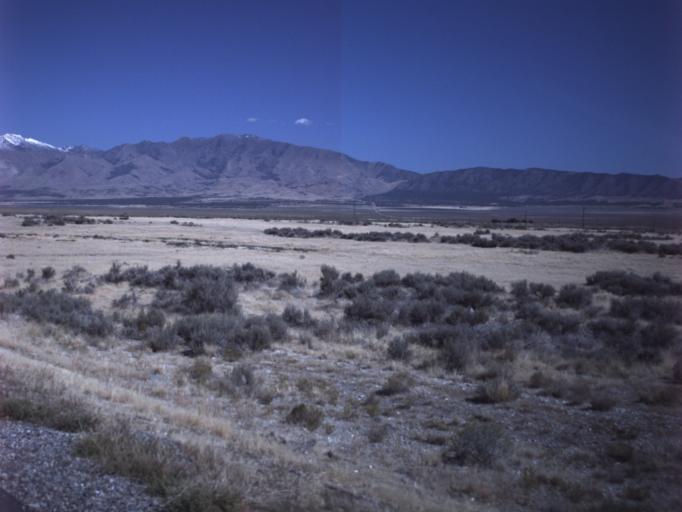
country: US
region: Utah
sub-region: Tooele County
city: Grantsville
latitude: 40.2340
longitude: -112.7233
